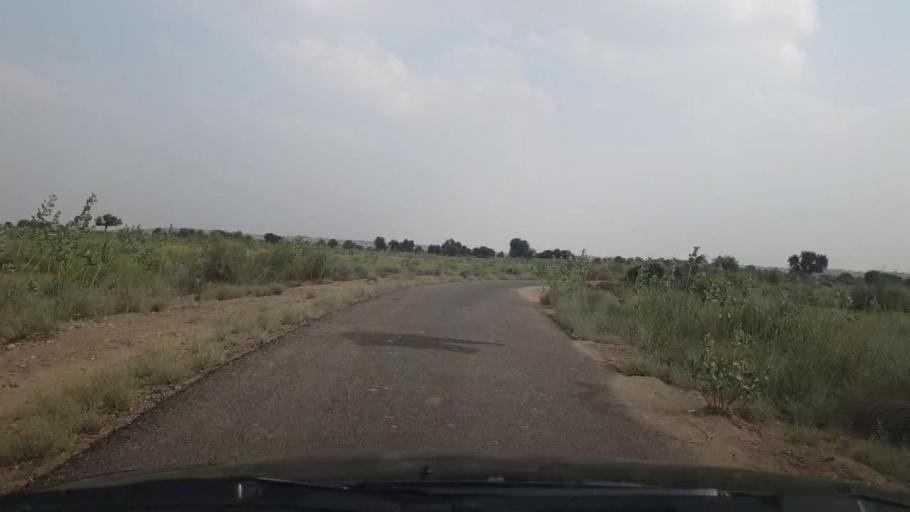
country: PK
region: Sindh
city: Islamkot
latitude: 25.0122
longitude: 70.5948
